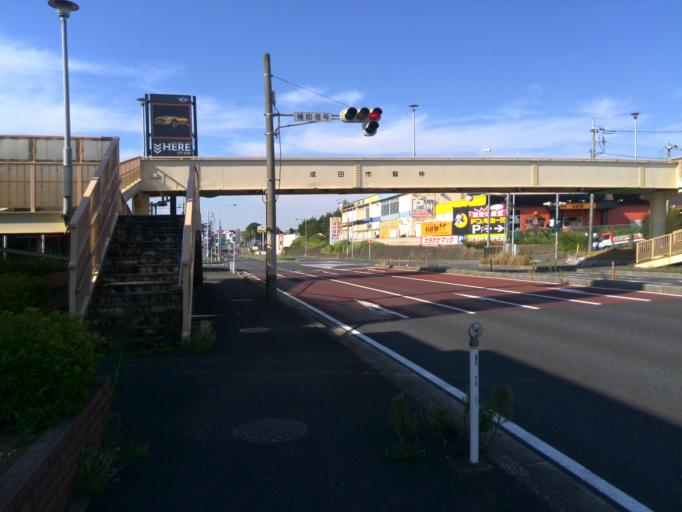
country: JP
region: Chiba
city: Narita
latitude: 35.7547
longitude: 140.3018
